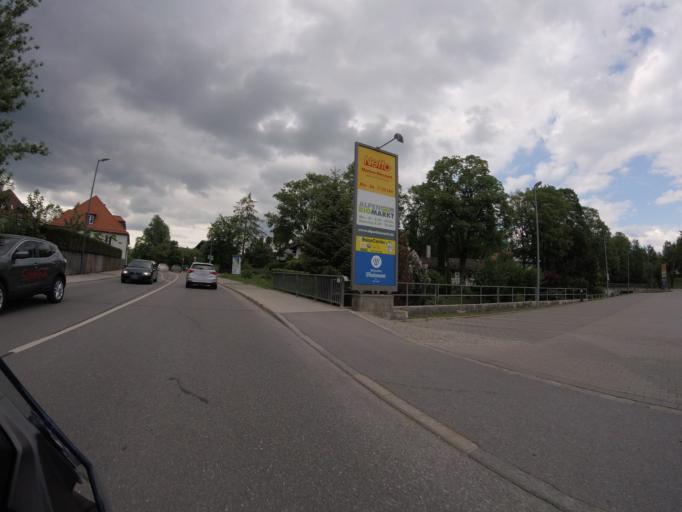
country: DE
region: Bavaria
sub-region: Upper Bavaria
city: Bad Toelz
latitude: 47.7607
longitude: 11.5695
